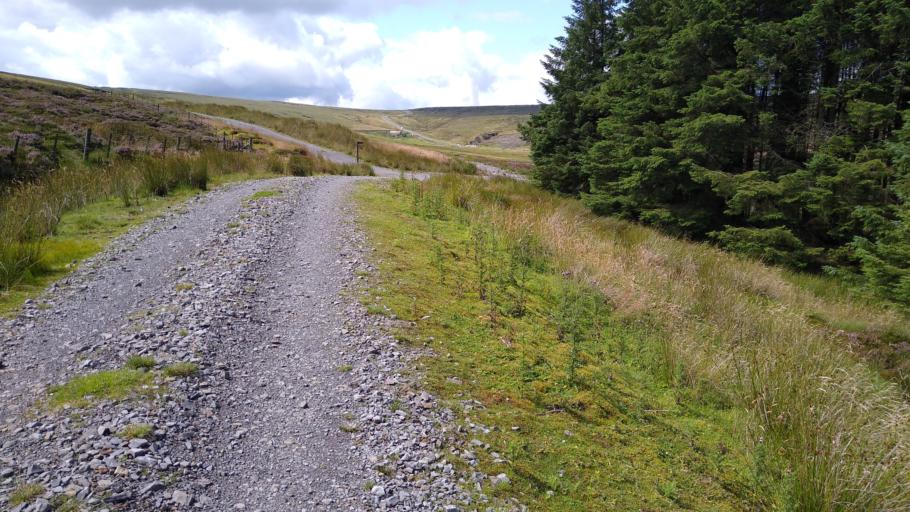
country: GB
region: England
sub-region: Northumberland
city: Bardon Mill
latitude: 54.7818
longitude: -2.2857
